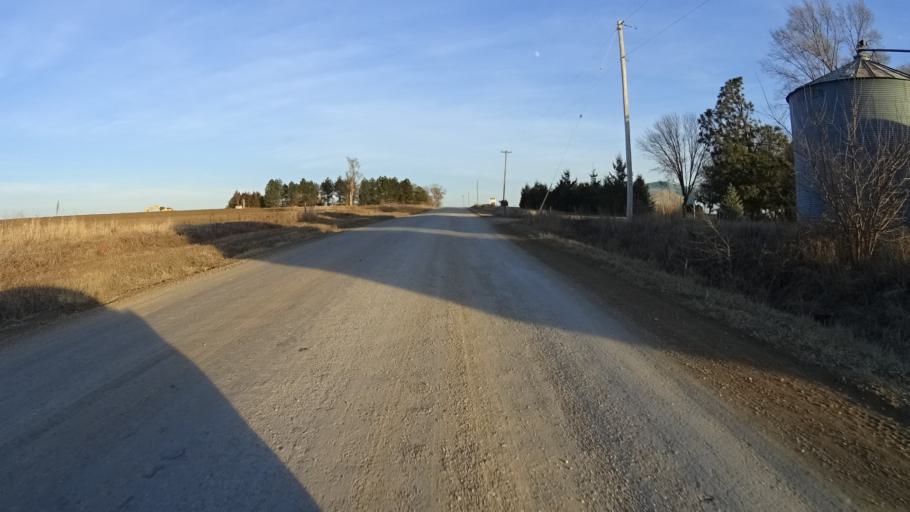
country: US
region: Nebraska
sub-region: Sarpy County
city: Springfield
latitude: 41.1326
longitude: -96.1075
